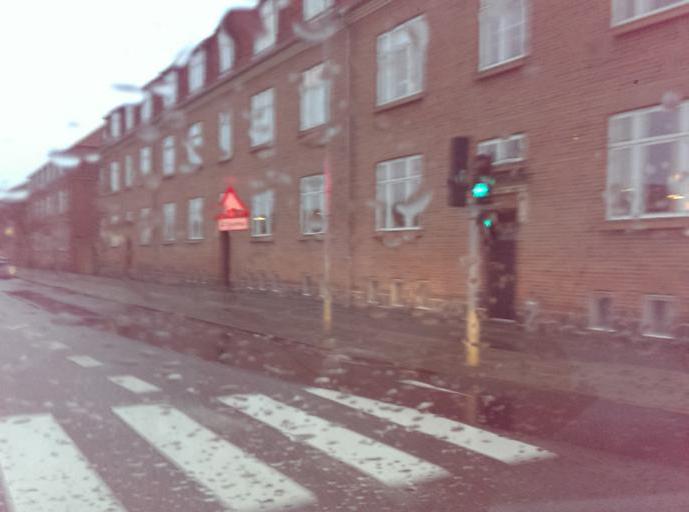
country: DK
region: South Denmark
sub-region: Esbjerg Kommune
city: Esbjerg
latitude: 55.4744
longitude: 8.4616
